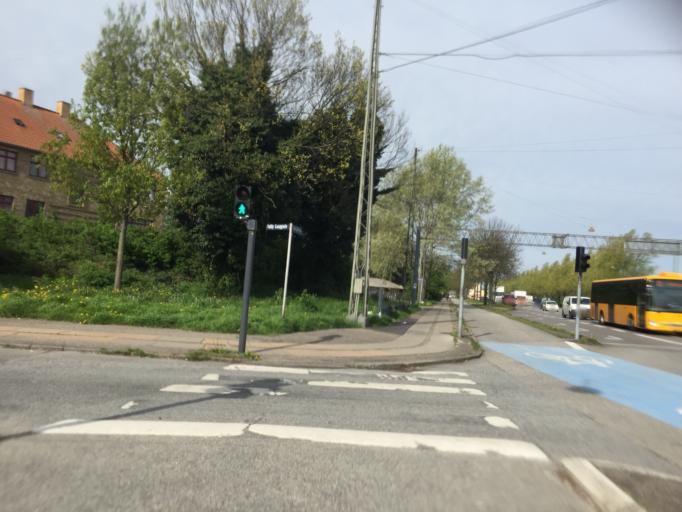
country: DK
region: Capital Region
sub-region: Kobenhavn
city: Vanlose
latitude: 55.6725
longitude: 12.4825
